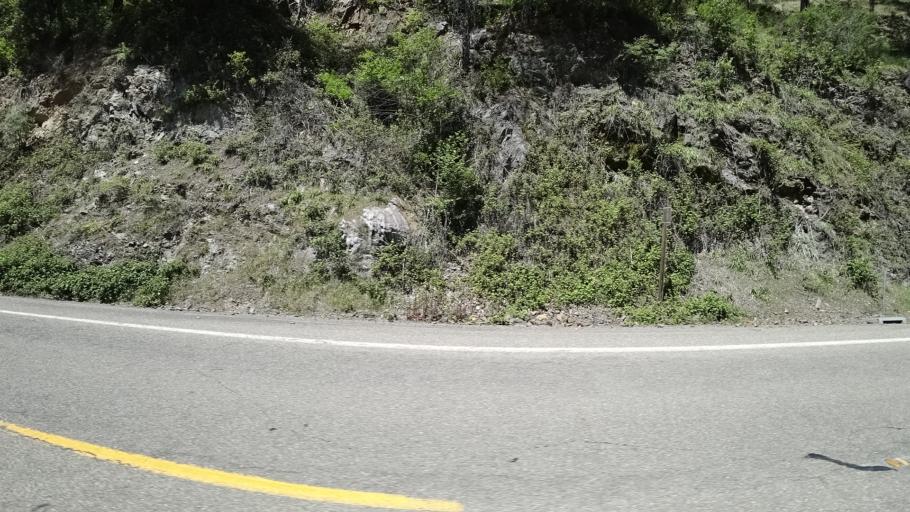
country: US
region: California
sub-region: Trinity County
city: Hayfork
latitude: 40.7678
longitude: -123.2970
